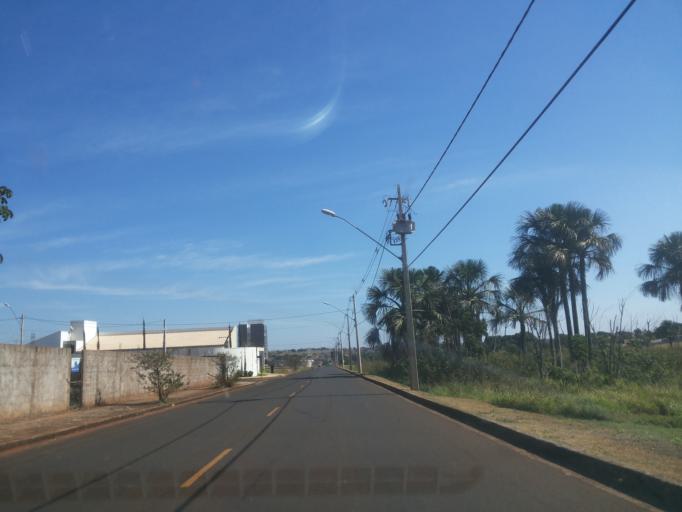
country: BR
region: Minas Gerais
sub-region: Ituiutaba
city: Ituiutaba
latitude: -19.0009
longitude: -49.4604
